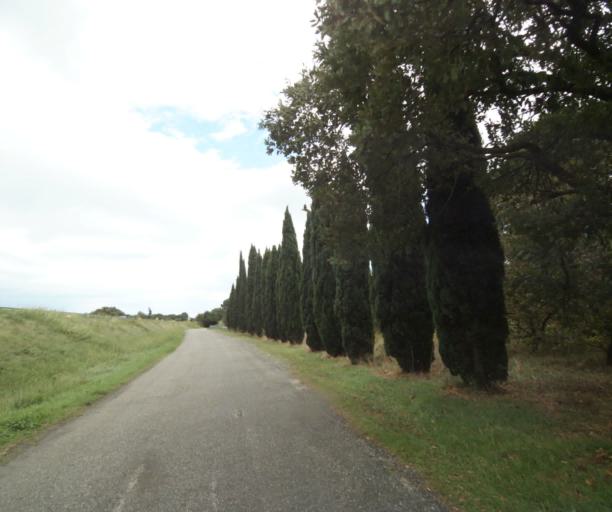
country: FR
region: Languedoc-Roussillon
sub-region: Departement des Pyrenees-Orientales
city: Argelers
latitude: 42.5422
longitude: 3.0131
